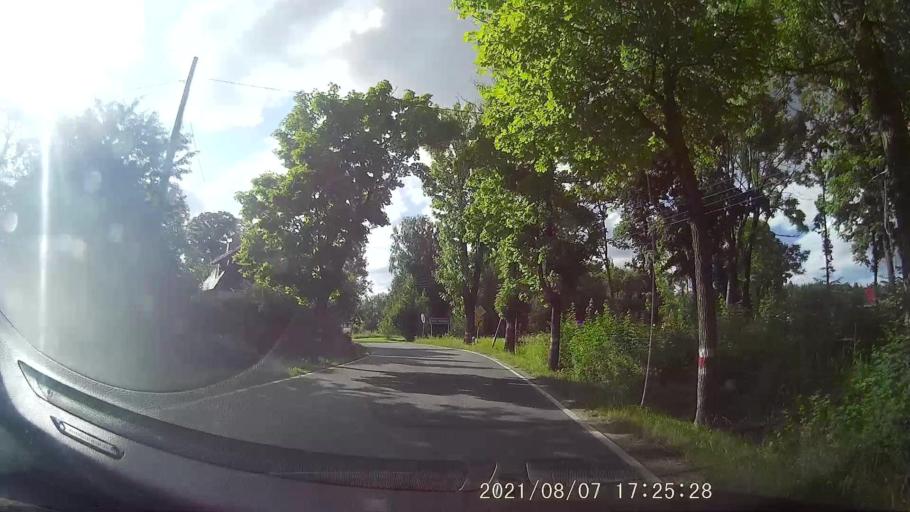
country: PL
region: Lower Silesian Voivodeship
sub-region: Powiat klodzki
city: Polanica-Zdroj
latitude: 50.3773
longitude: 16.5311
